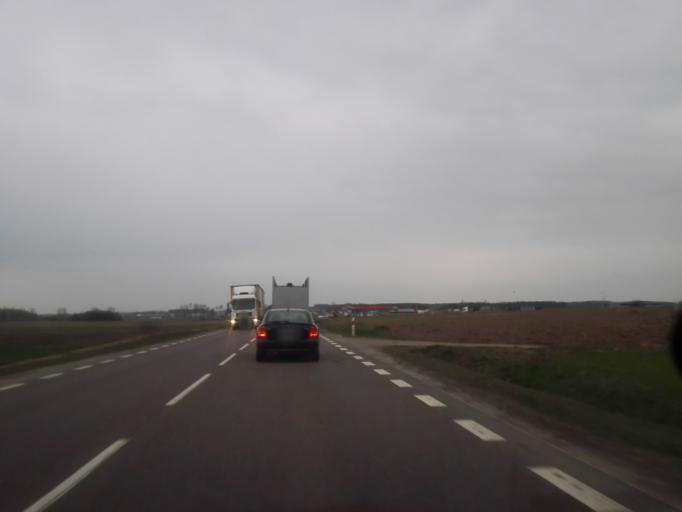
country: PL
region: Podlasie
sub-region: Powiat grajewski
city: Grajewo
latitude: 53.6308
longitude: 22.4187
